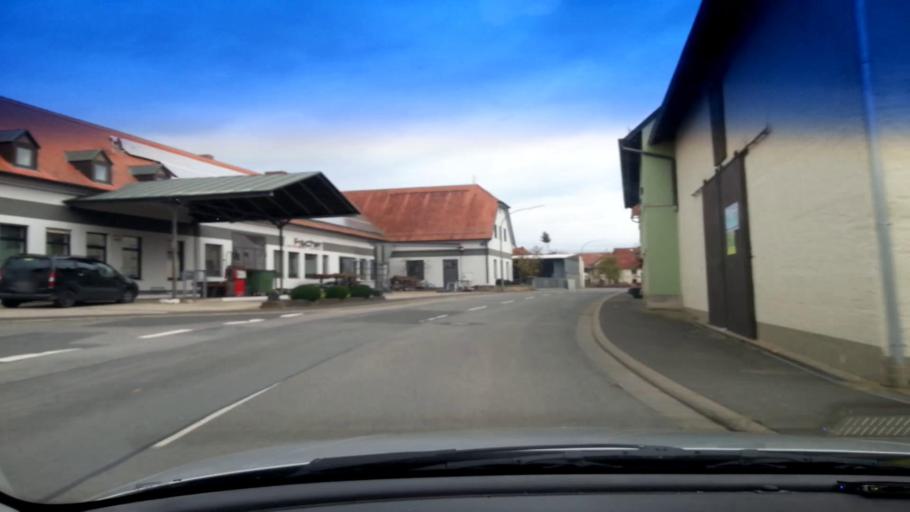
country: DE
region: Bavaria
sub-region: Regierungsbezirk Unterfranken
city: Stettfeld
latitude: 49.9456
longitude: 10.7488
